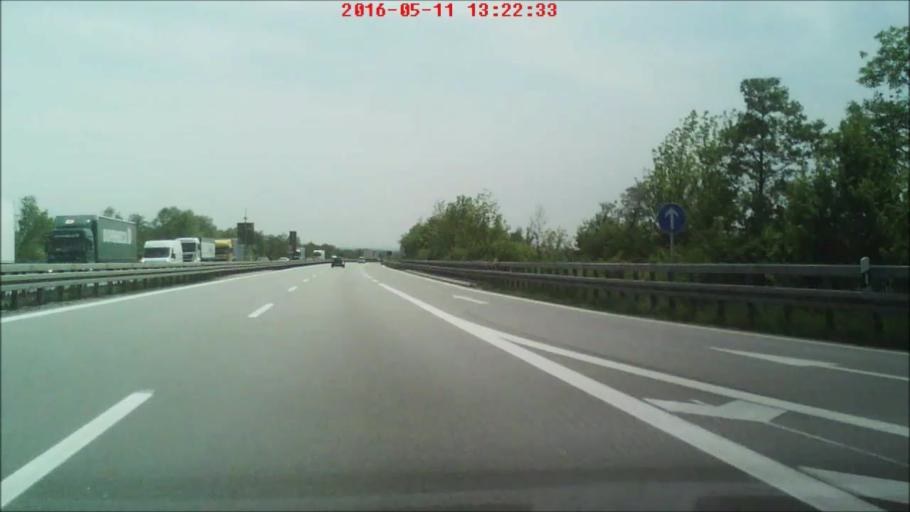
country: AT
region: Upper Austria
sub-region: Politischer Bezirk Scharding
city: Scharding
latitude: 48.4551
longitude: 13.3759
